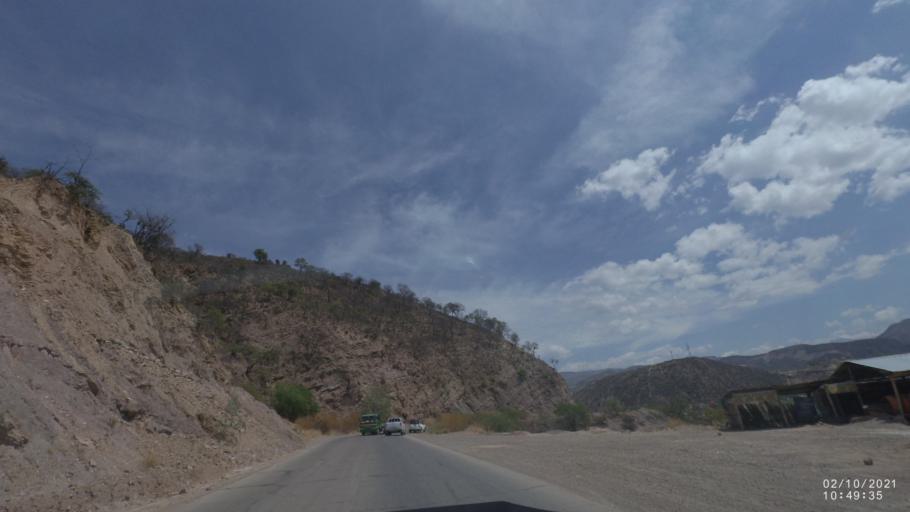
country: BO
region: Cochabamba
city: Sipe Sipe
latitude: -17.5789
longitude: -66.3453
